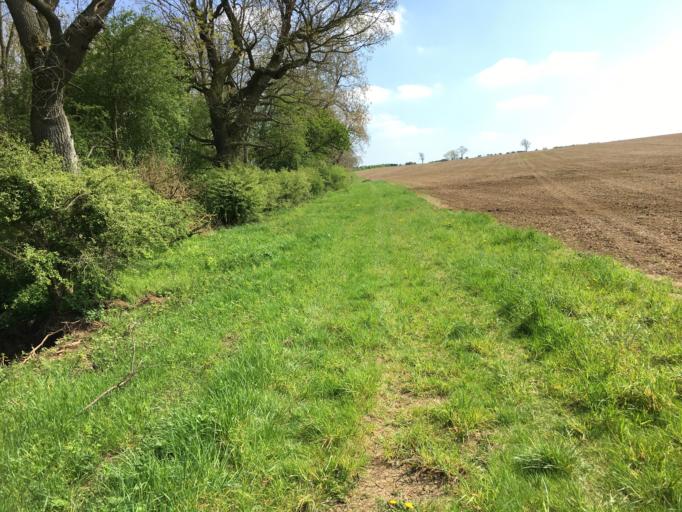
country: GB
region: England
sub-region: Leicestershire
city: Houghton on the Hill
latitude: 52.6130
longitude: -0.9908
